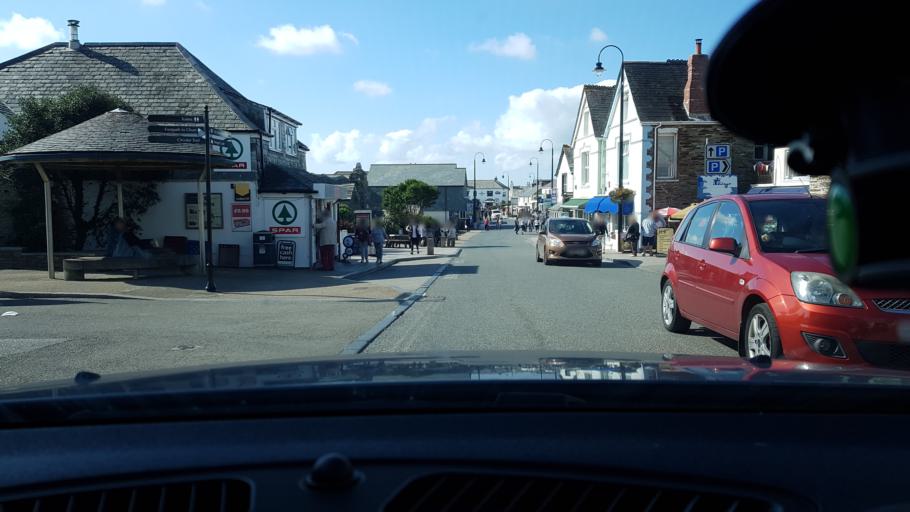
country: GB
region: England
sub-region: Cornwall
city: Tintagel
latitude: 50.6631
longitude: -4.7508
